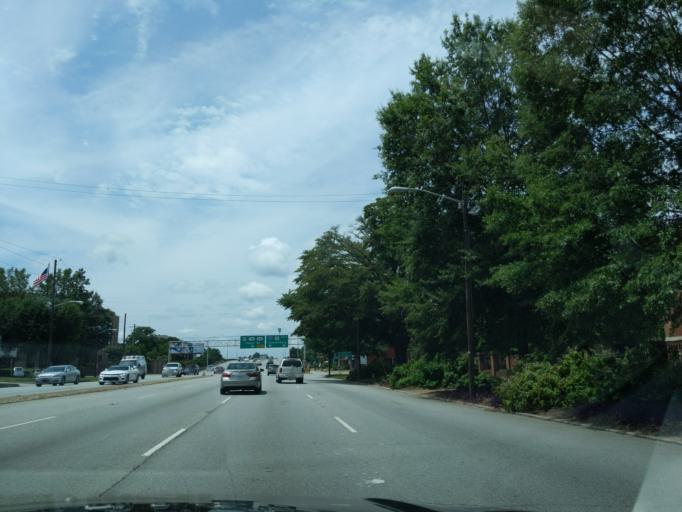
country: US
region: South Carolina
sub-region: Richland County
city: Columbia
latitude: 34.0118
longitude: -81.0444
